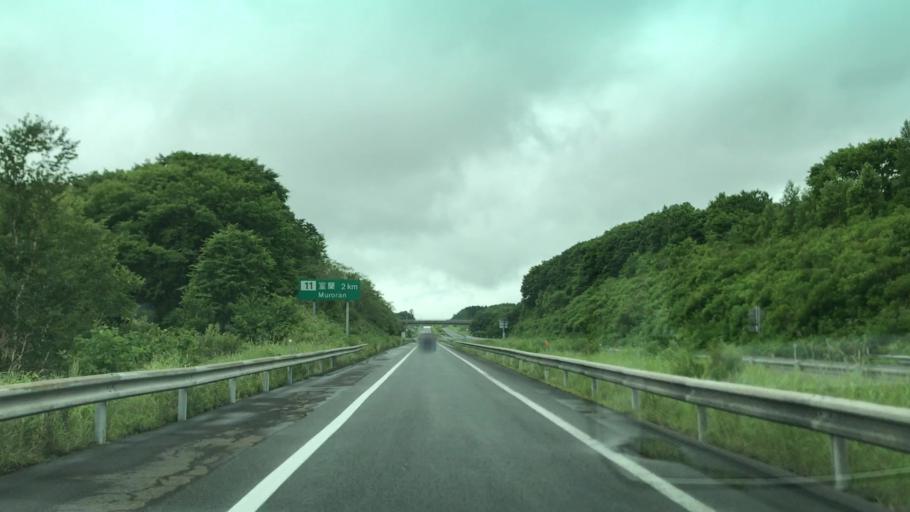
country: JP
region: Hokkaido
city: Muroran
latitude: 42.3837
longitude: 140.9977
